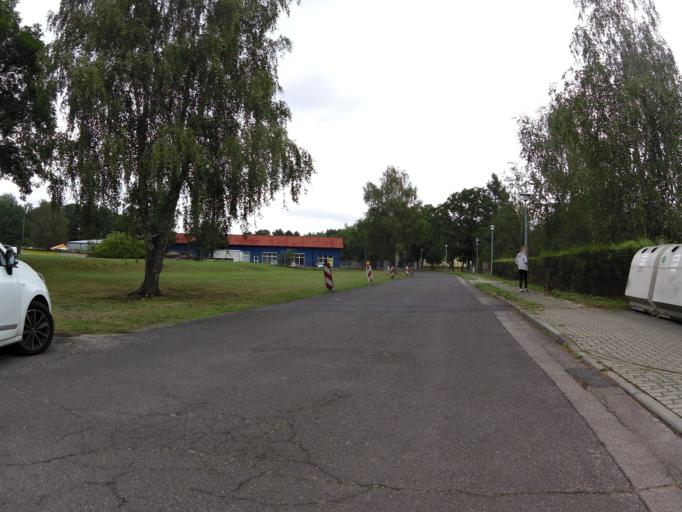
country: DE
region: Brandenburg
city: Storkow
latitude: 52.2664
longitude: 13.9478
